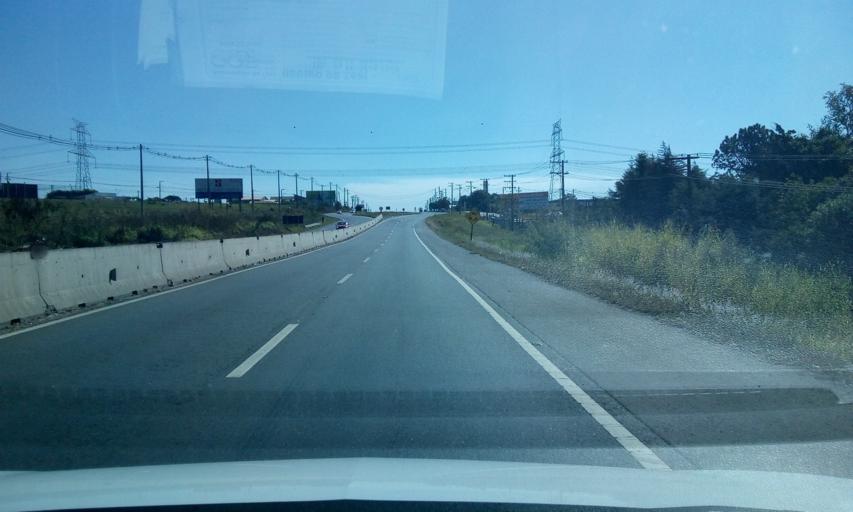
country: BR
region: Sao Paulo
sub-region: Itupeva
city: Itupeva
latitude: -23.1696
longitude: -47.0005
